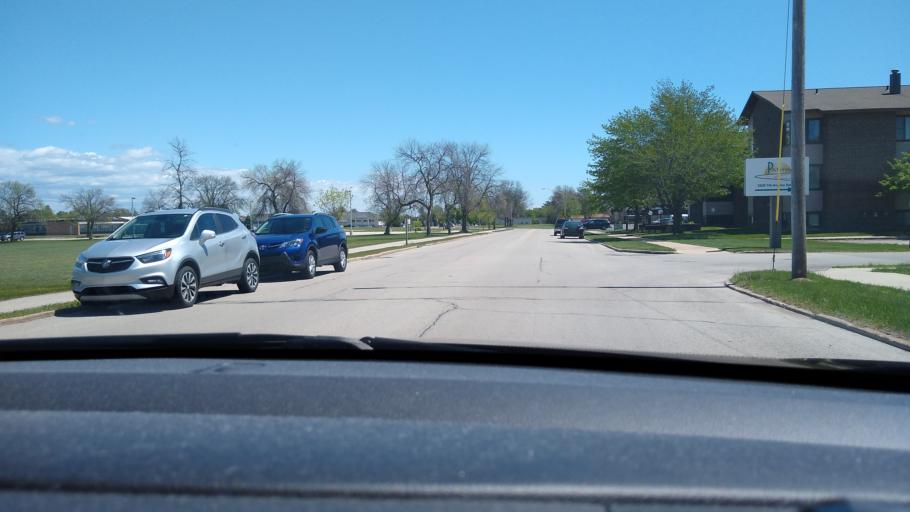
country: US
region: Michigan
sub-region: Delta County
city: Escanaba
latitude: 45.7391
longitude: -87.0841
